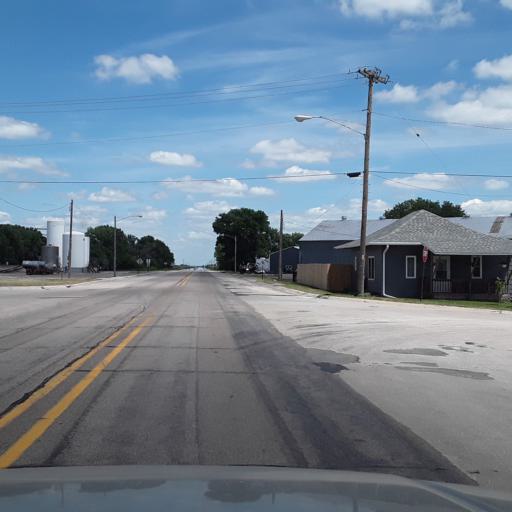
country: US
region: Nebraska
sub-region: Platte County
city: Columbus
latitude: 41.3881
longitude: -97.4937
